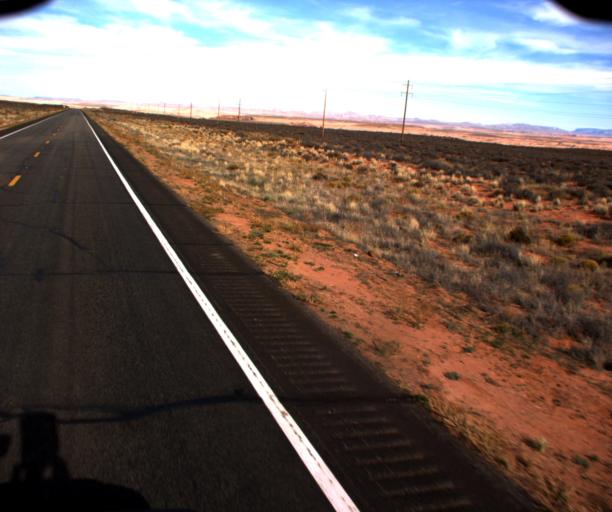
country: US
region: Arizona
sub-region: Navajo County
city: Kayenta
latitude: 36.9221
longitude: -109.7619
